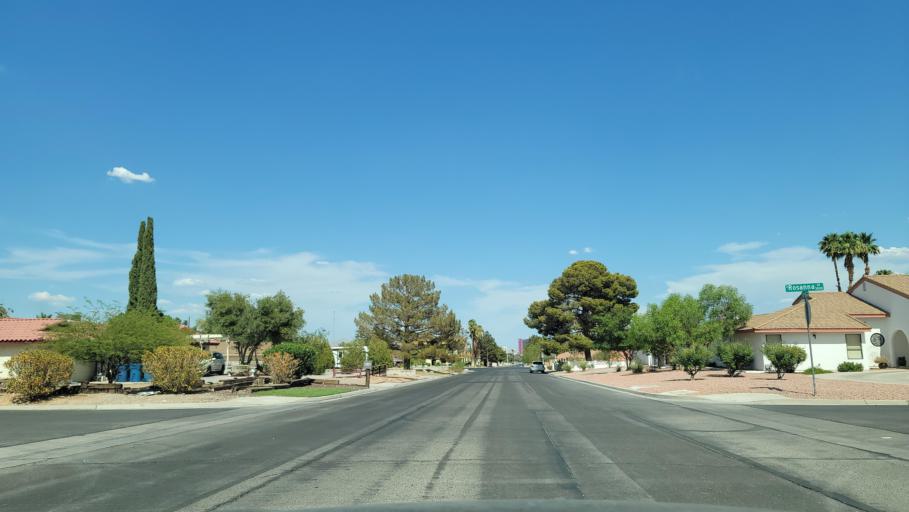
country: US
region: Nevada
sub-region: Clark County
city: Spring Valley
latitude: 36.1349
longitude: -115.2454
